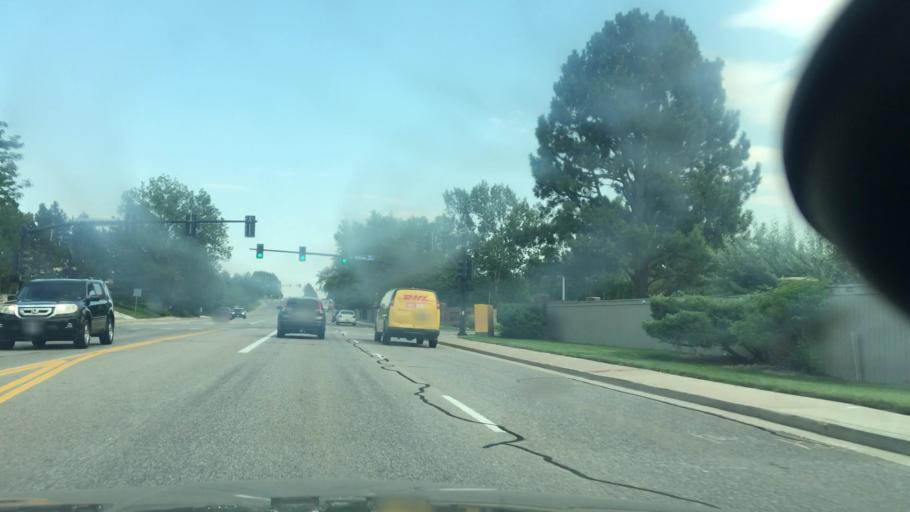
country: US
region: Colorado
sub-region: Arapahoe County
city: Castlewood
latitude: 39.5806
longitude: -104.8900
